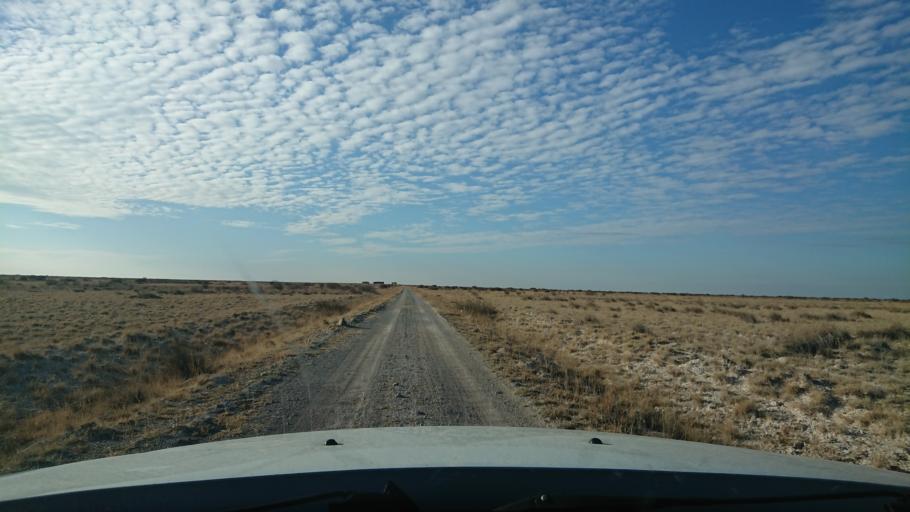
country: TR
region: Aksaray
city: Eskil
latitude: 38.5437
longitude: 33.3277
